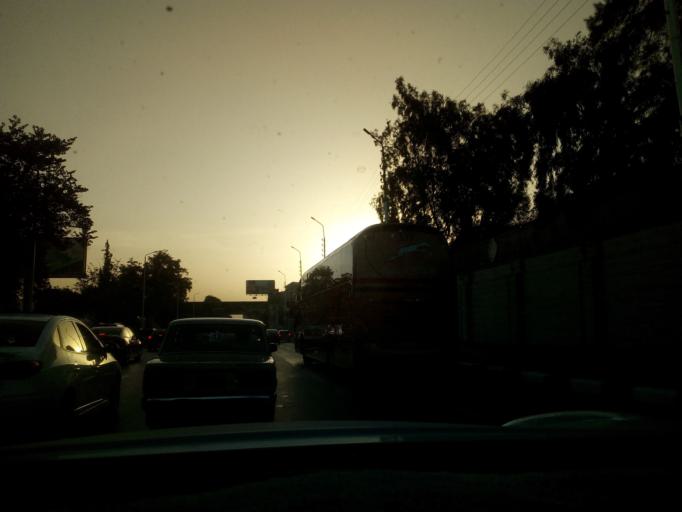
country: EG
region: Muhafazat al Qahirah
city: Cairo
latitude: 30.1011
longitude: 31.3521
